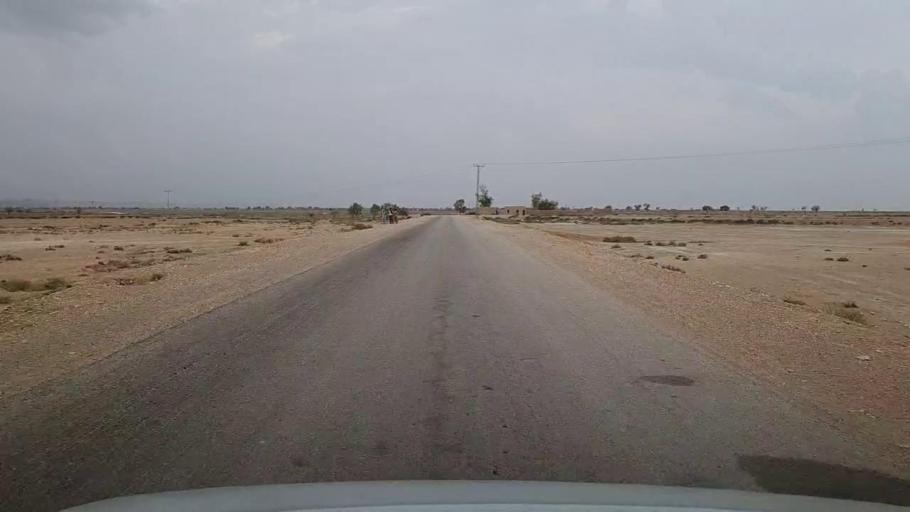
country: PK
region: Sindh
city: Sehwan
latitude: 26.3369
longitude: 67.7149
